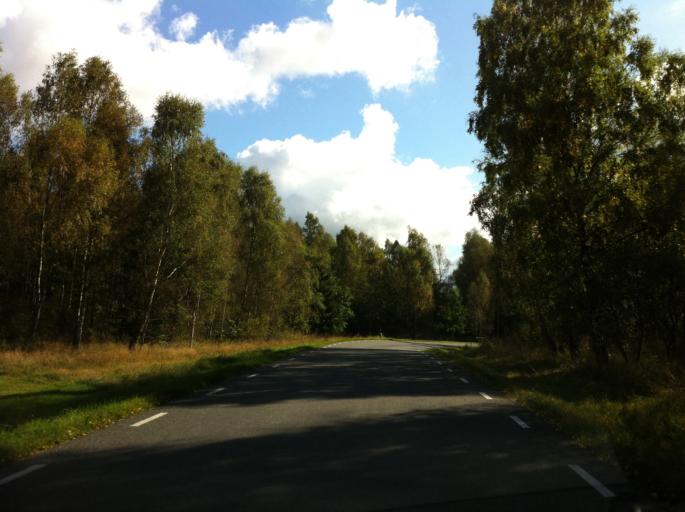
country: SE
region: Skane
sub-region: Kristianstads Kommun
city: Degeberga
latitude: 55.7423
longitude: 13.9391
